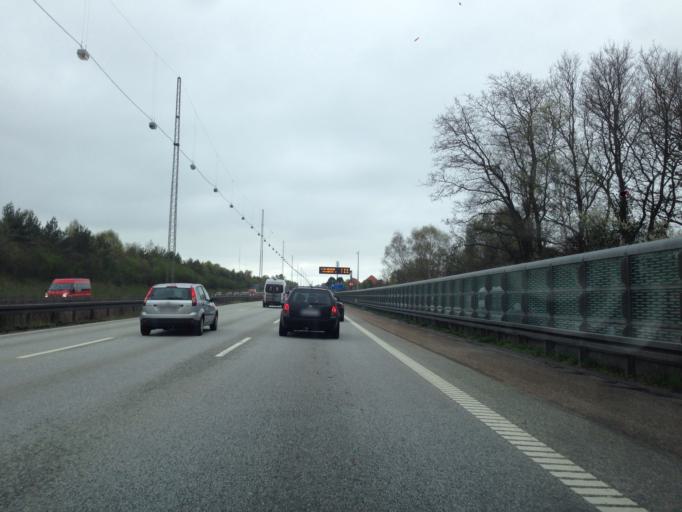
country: DK
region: Capital Region
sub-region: Rudersdal Kommune
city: Trorod
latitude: 55.8086
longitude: 12.5320
